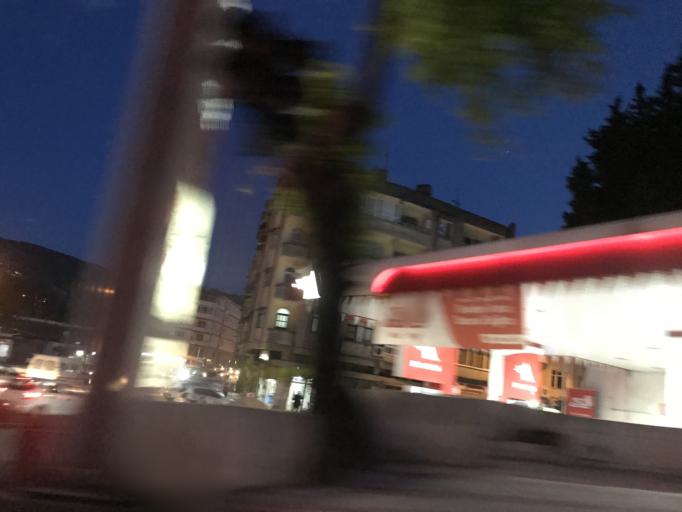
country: TR
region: Hatay
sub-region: Antakya Ilcesi
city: Antakya
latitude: 36.1996
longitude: 36.1538
